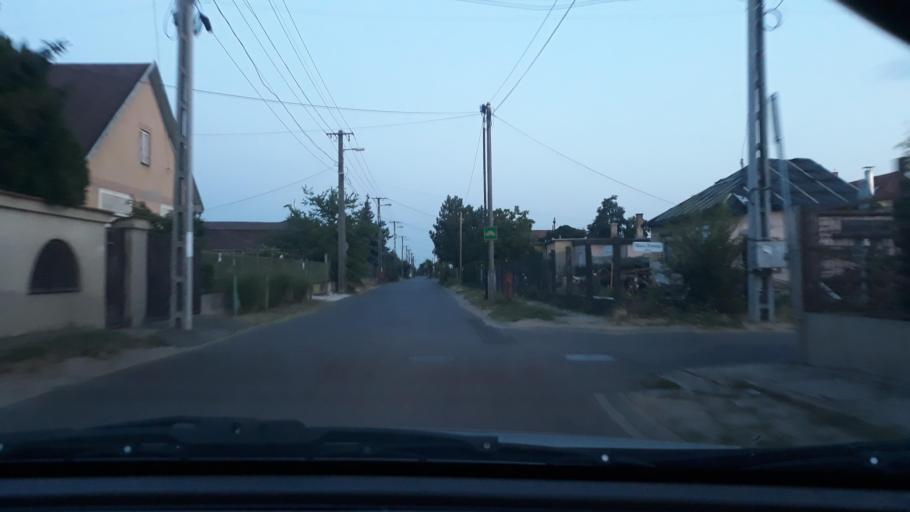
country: HU
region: Hajdu-Bihar
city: Debrecen
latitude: 47.5379
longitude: 21.6660
